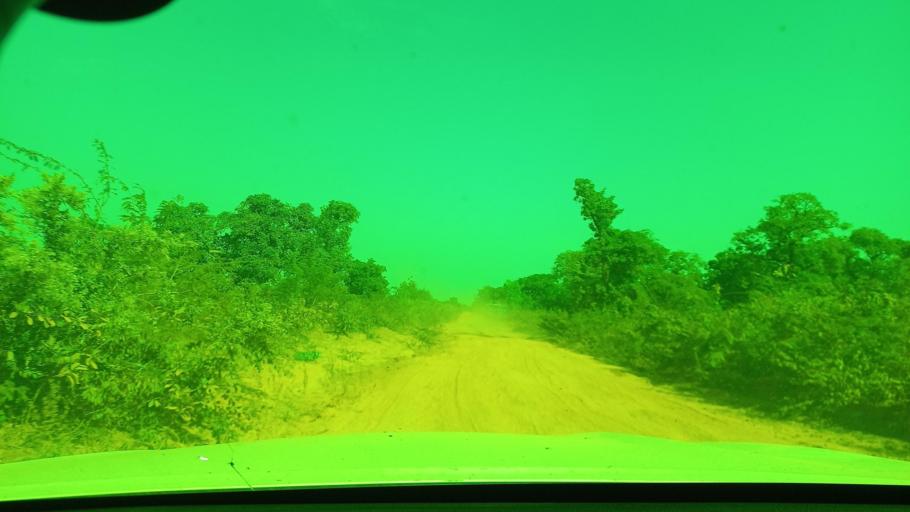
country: ML
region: Bamako
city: Bamako
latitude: 12.3968
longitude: -7.9845
